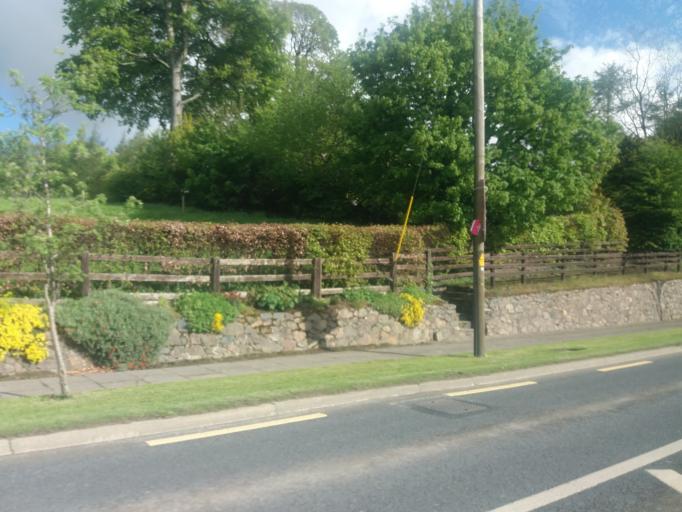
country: IE
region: Leinster
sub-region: Loch Garman
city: Ferns
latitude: 52.5915
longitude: -6.4906
